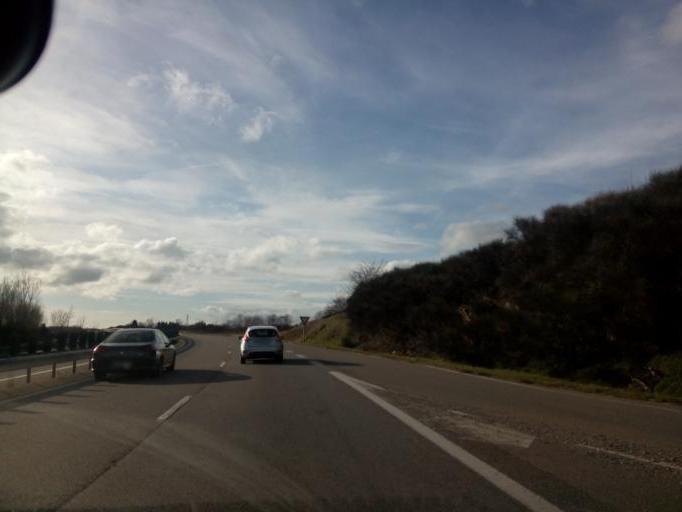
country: FR
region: Rhone-Alpes
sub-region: Departement de l'Ardeche
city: Peaugres
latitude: 45.3016
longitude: 4.7355
